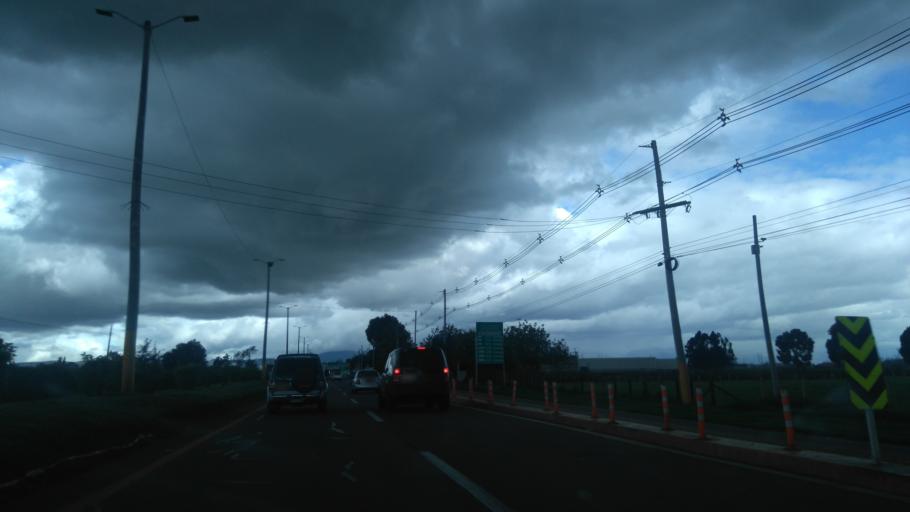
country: CO
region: Cundinamarca
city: Funza
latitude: 4.7832
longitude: -74.1888
